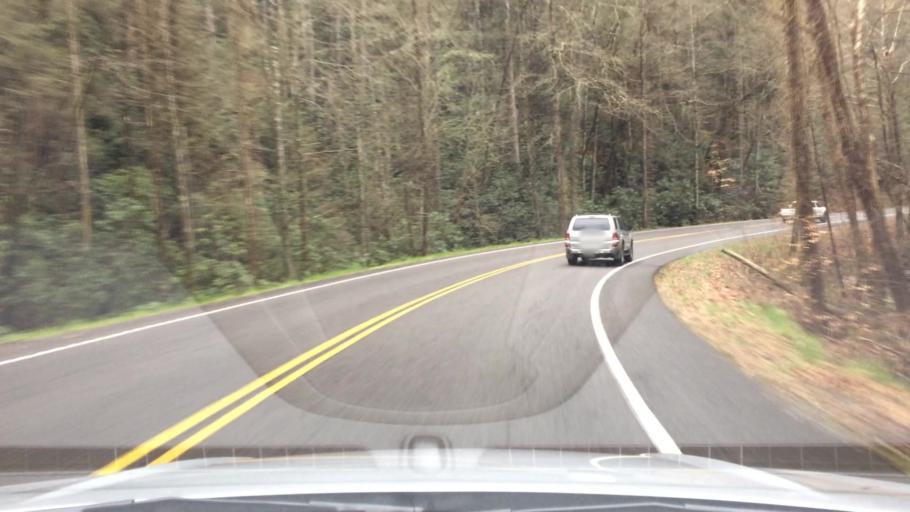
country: US
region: Georgia
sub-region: Fannin County
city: McCaysville
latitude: 35.1873
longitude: -84.3213
